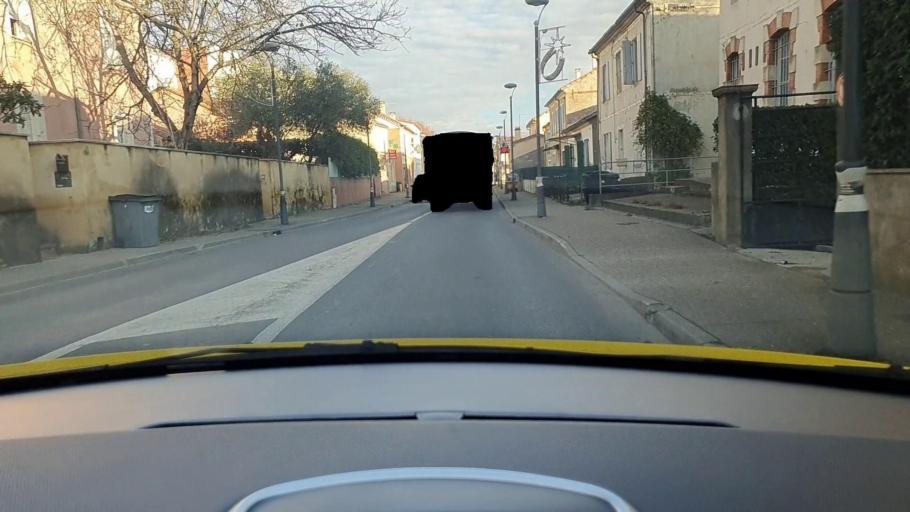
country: FR
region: Languedoc-Roussillon
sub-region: Departement du Gard
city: Saint-Martin-de-Valgalgues
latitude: 44.1598
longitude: 4.0829
